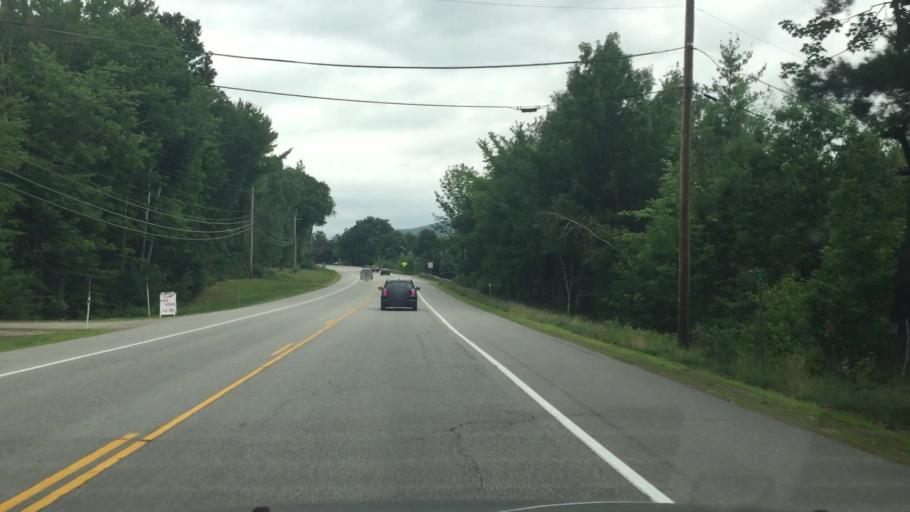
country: US
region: New Hampshire
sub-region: Carroll County
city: Center Harbor
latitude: 43.7005
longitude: -71.4604
